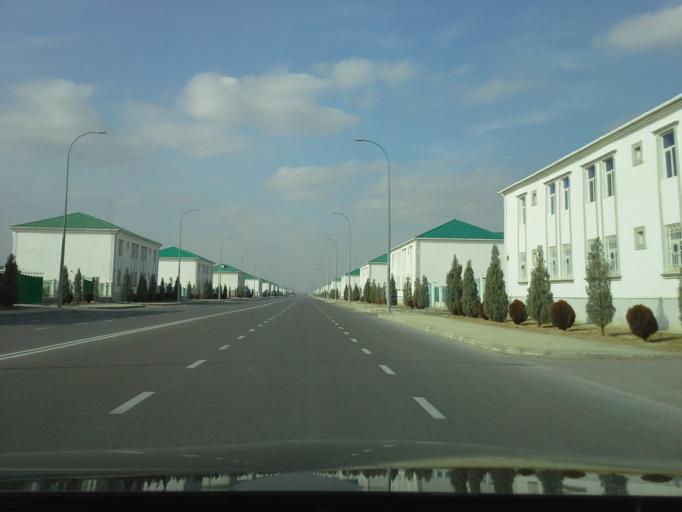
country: TM
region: Ahal
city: Abadan
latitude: 38.0779
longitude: 58.2795
